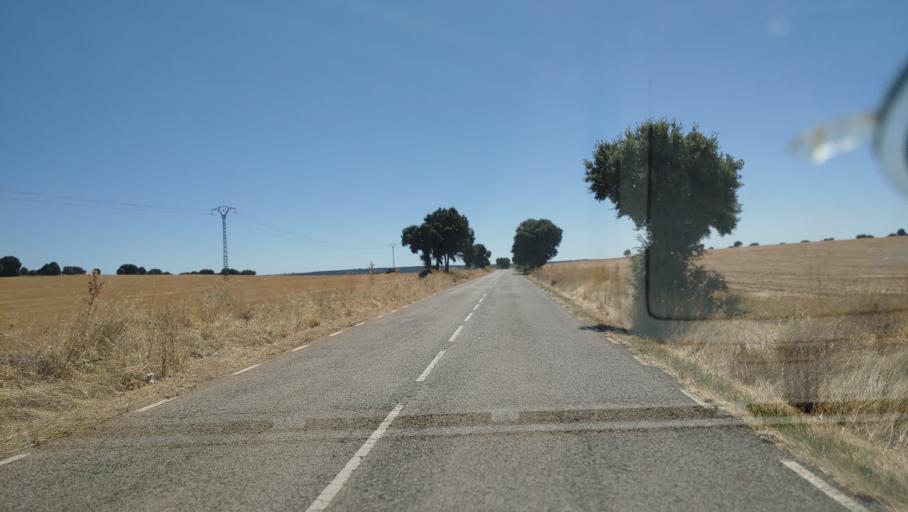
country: ES
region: Castille-La Mancha
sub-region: Provincia de Albacete
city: Ossa de Montiel
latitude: 38.9162
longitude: -2.7584
